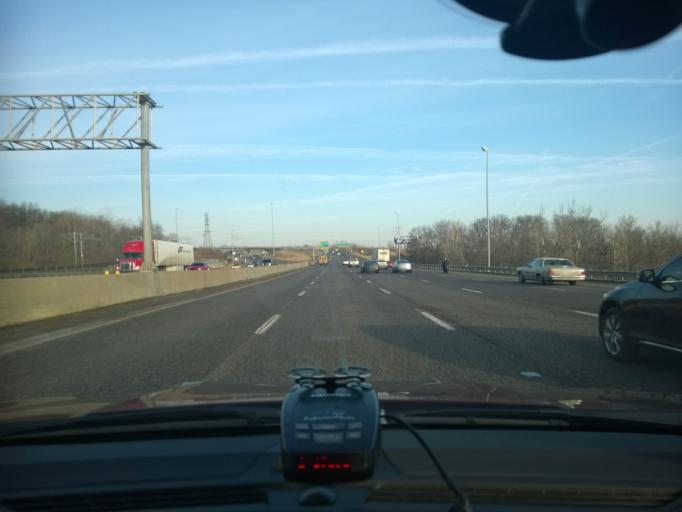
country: US
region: Missouri
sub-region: Saint Louis County
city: Cool Valley
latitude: 38.7258
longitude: -90.3263
